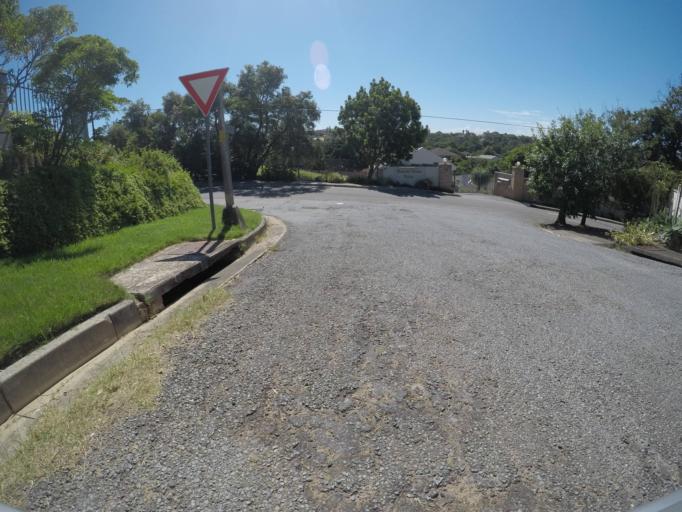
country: ZA
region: Eastern Cape
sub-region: Buffalo City Metropolitan Municipality
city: East London
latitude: -32.9830
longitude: 27.9274
